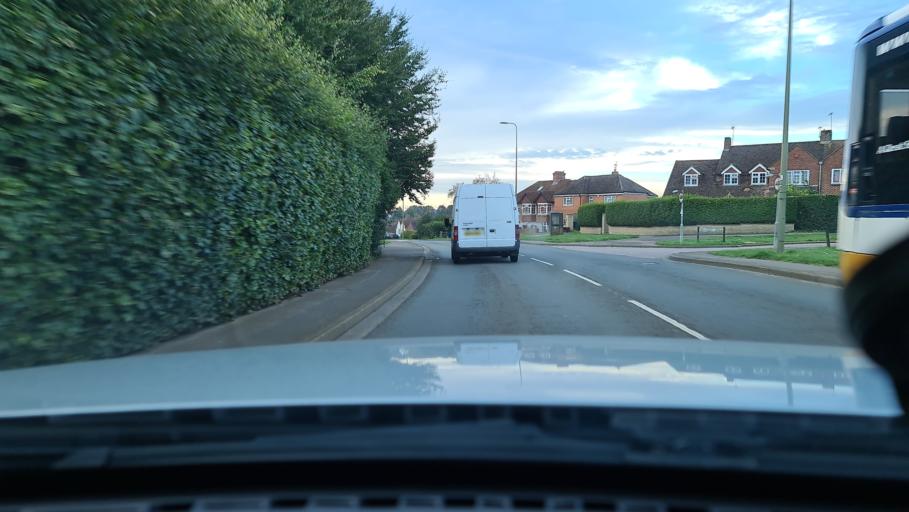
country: GB
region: England
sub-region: Oxfordshire
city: Banbury
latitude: 52.0686
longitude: -1.3605
